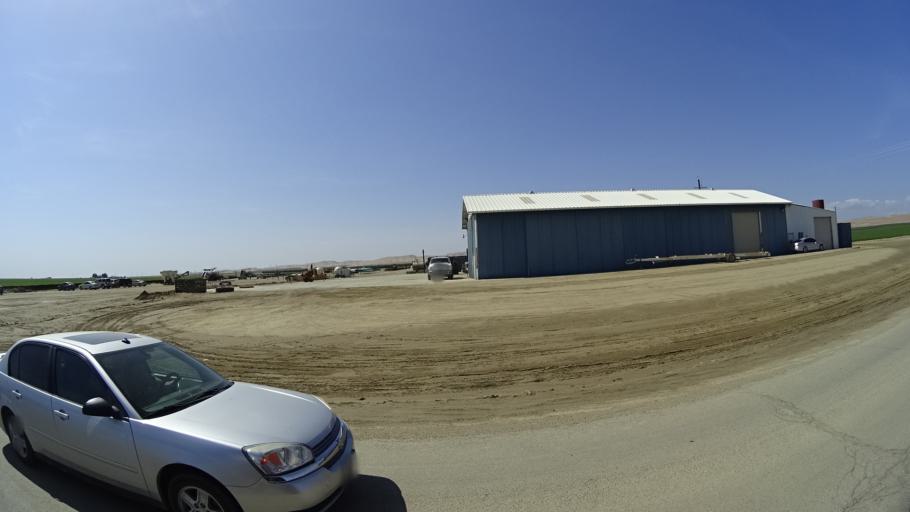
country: US
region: California
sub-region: Kings County
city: Avenal
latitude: 36.0726
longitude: -120.0478
